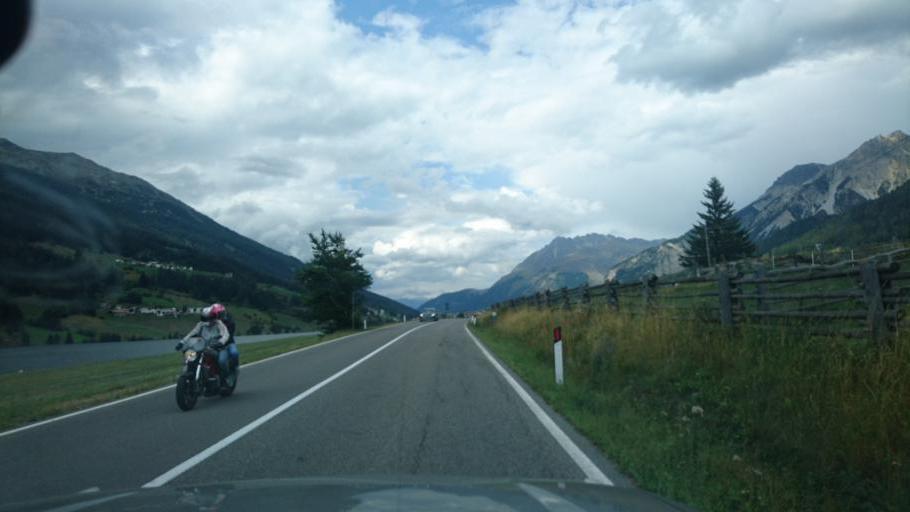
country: IT
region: Trentino-Alto Adige
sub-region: Bolzano
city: Curon Venosta
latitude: 46.7501
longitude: 10.5358
